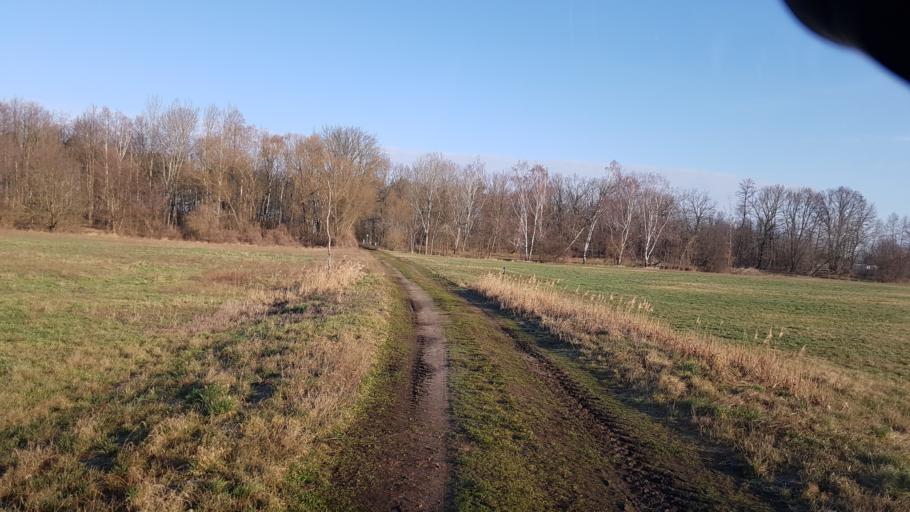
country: DE
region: Brandenburg
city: Lubbenau
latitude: 51.8235
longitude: 13.9106
